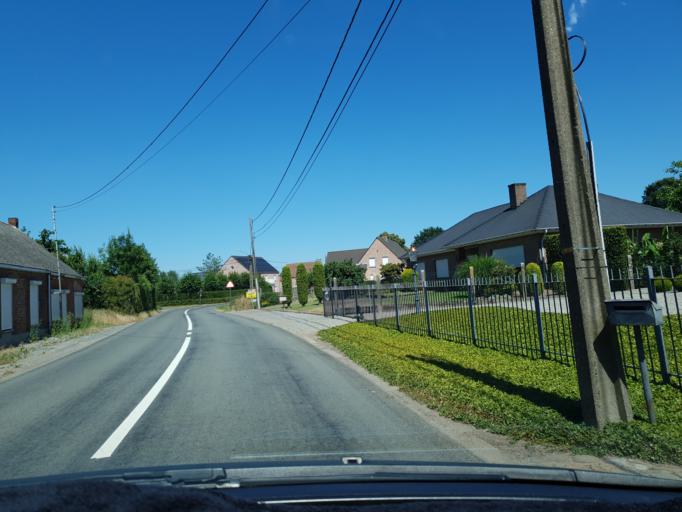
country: BE
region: Flanders
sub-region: Provincie Antwerpen
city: Geel
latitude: 51.1560
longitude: 4.9384
